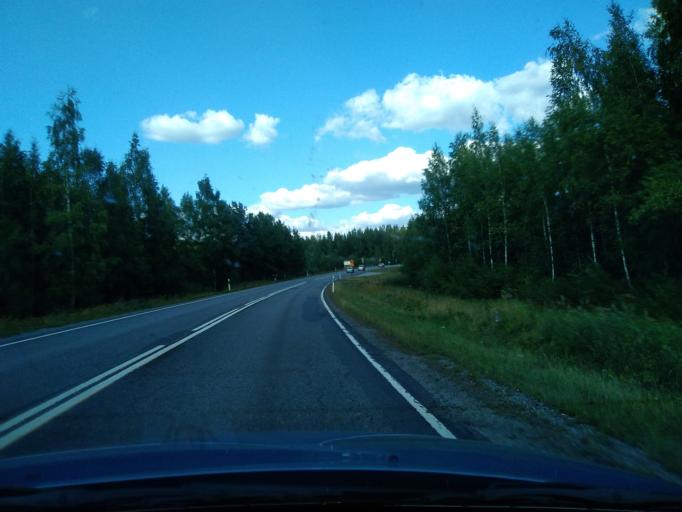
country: FI
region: Pirkanmaa
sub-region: Ylae-Pirkanmaa
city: Maenttae
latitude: 62.0012
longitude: 24.6420
